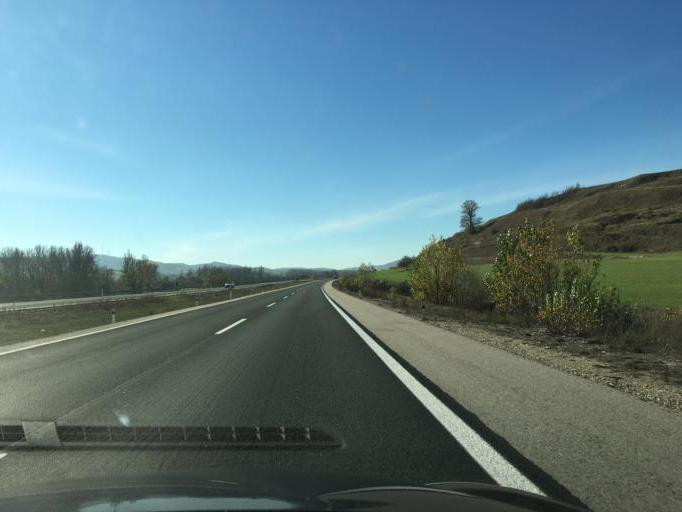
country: ES
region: Castille and Leon
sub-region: Provincia de Burgos
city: Castil de Peones
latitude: 42.4899
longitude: -3.3811
